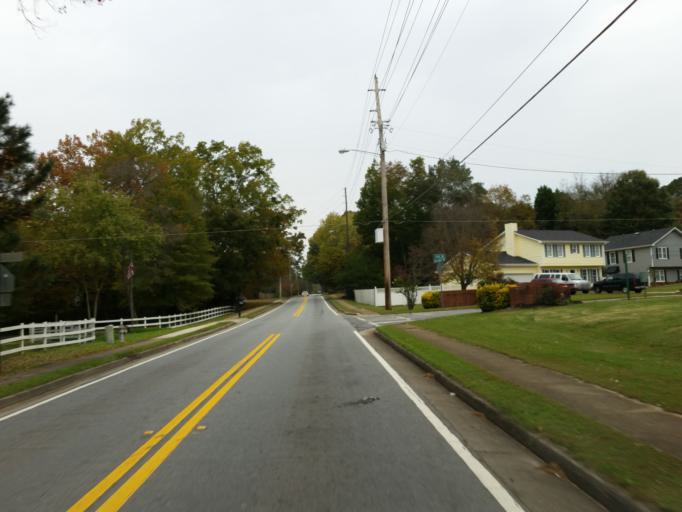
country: US
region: Georgia
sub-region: Cherokee County
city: Woodstock
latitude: 34.0522
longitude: -84.5088
